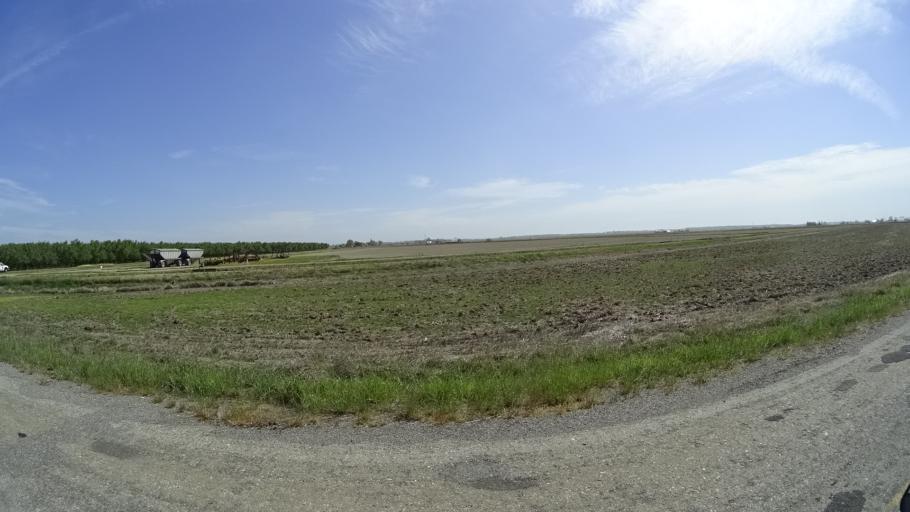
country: US
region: California
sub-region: Glenn County
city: Hamilton City
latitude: 39.6082
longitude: -122.0464
